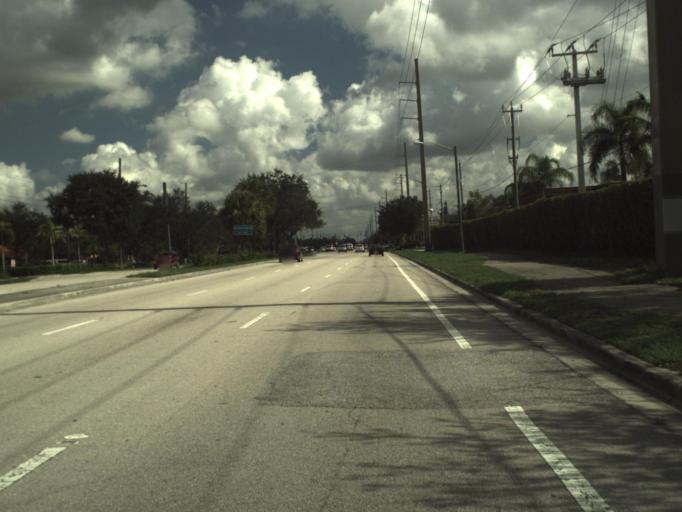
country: US
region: Florida
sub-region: Palm Beach County
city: Greenacres City
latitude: 26.6473
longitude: -80.1454
